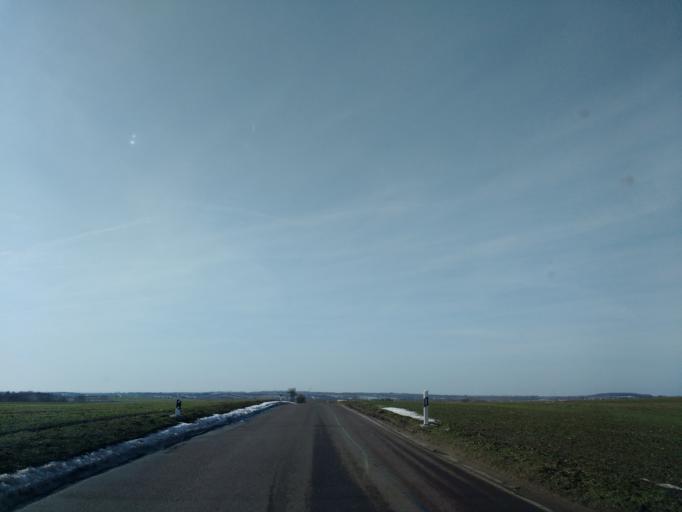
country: DE
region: Saxony-Anhalt
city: Gutenberg
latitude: 51.5528
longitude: 11.9915
